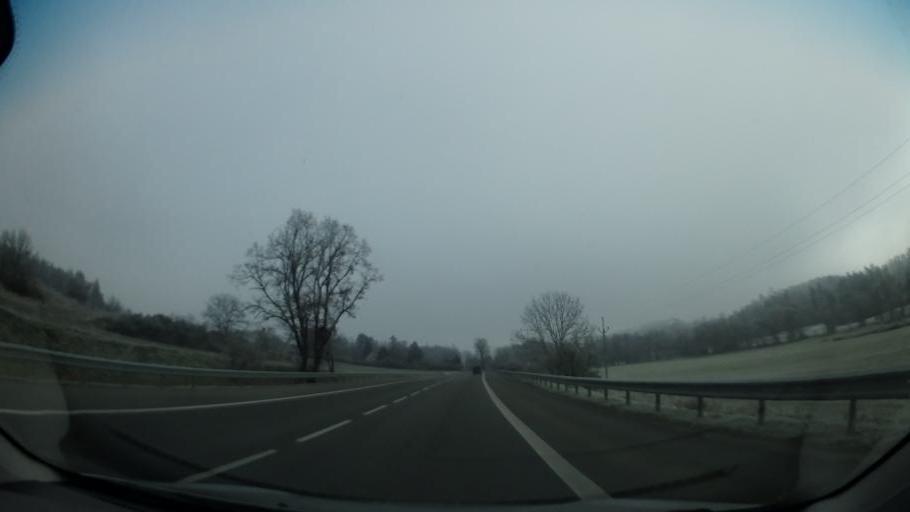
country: CZ
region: Vysocina
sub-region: Okres Trebic
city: Trebic
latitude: 49.2151
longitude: 15.9235
